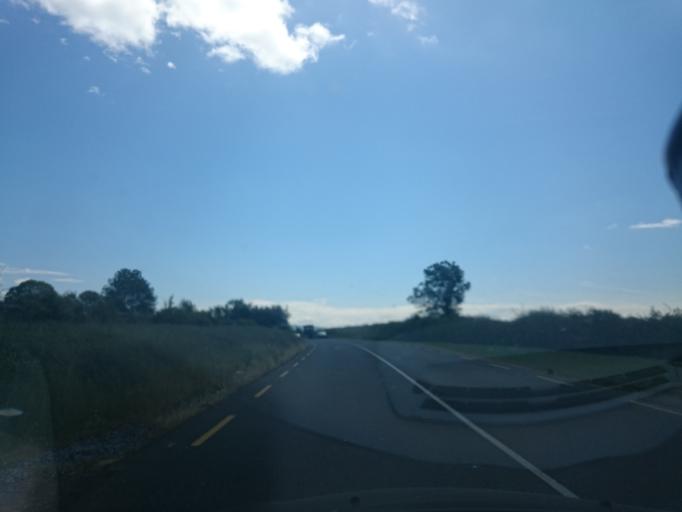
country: IE
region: Leinster
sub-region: Kilkenny
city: Thomastown
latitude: 52.6416
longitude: -7.1077
